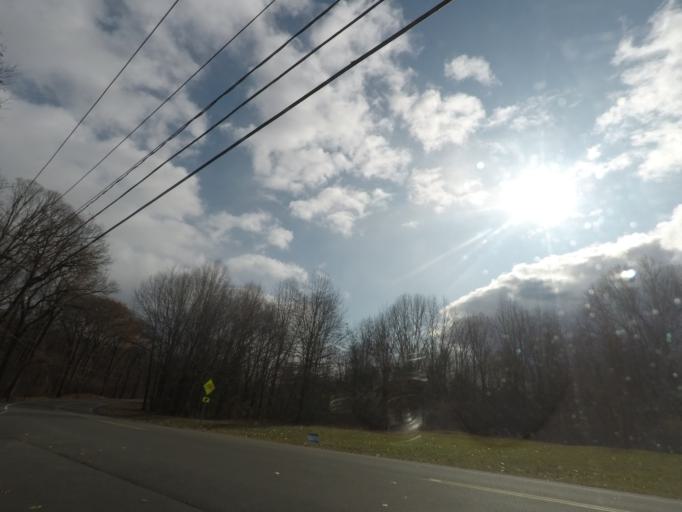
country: US
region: New York
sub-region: Saratoga County
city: Country Knolls
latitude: 42.9138
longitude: -73.8277
